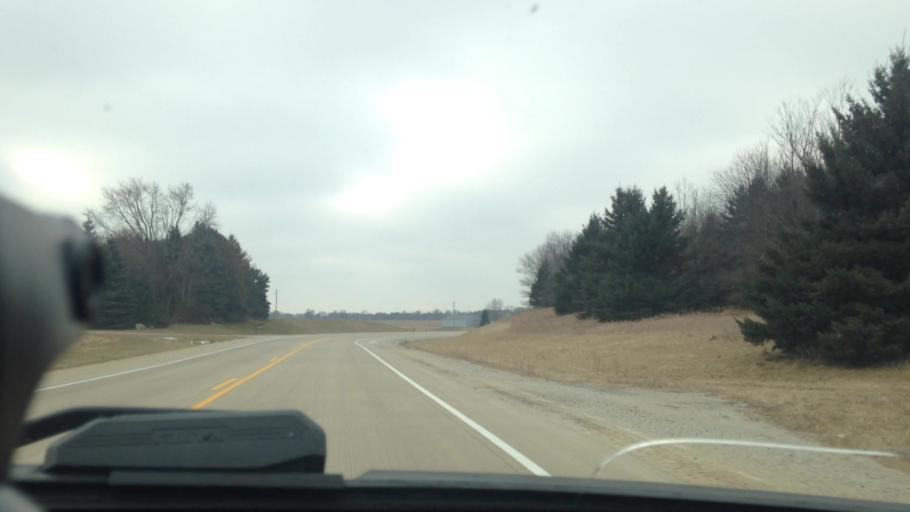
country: US
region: Wisconsin
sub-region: Dodge County
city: Beaver Dam
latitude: 43.4681
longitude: -88.7613
